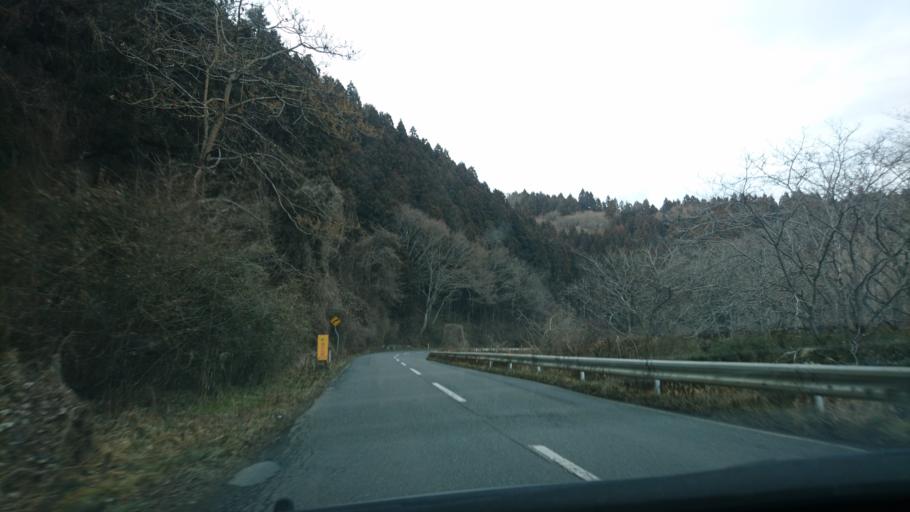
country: JP
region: Iwate
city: Ichinoseki
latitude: 38.8556
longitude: 141.3032
